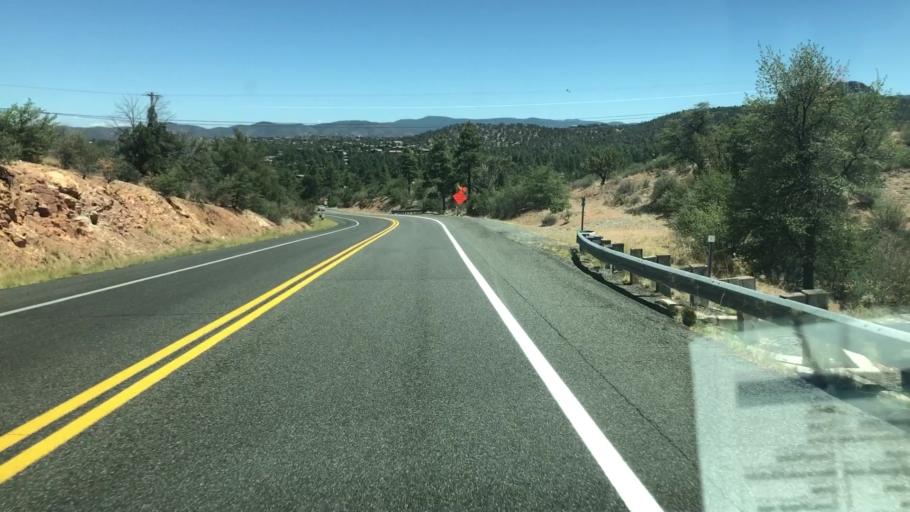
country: US
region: Arizona
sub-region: Yavapai County
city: Prescott
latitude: 34.5802
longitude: -112.5313
